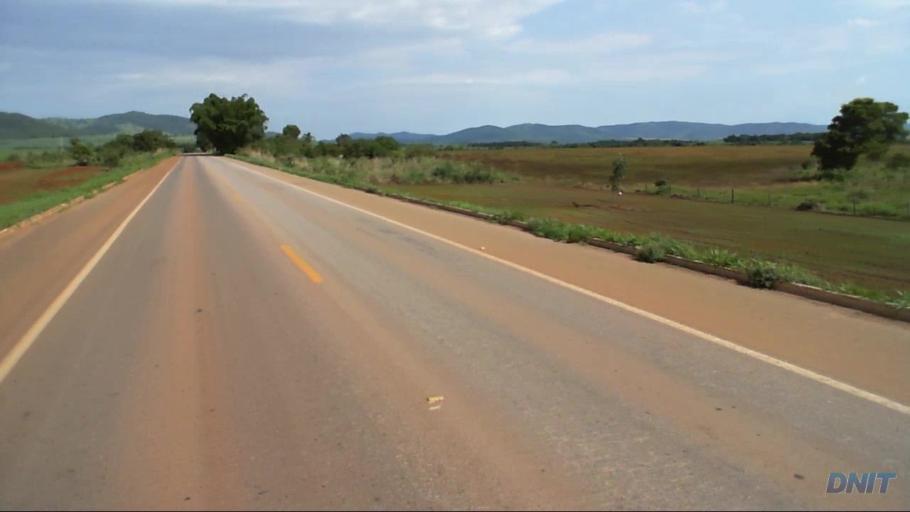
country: BR
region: Goias
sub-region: Barro Alto
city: Barro Alto
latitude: -15.0608
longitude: -48.8770
